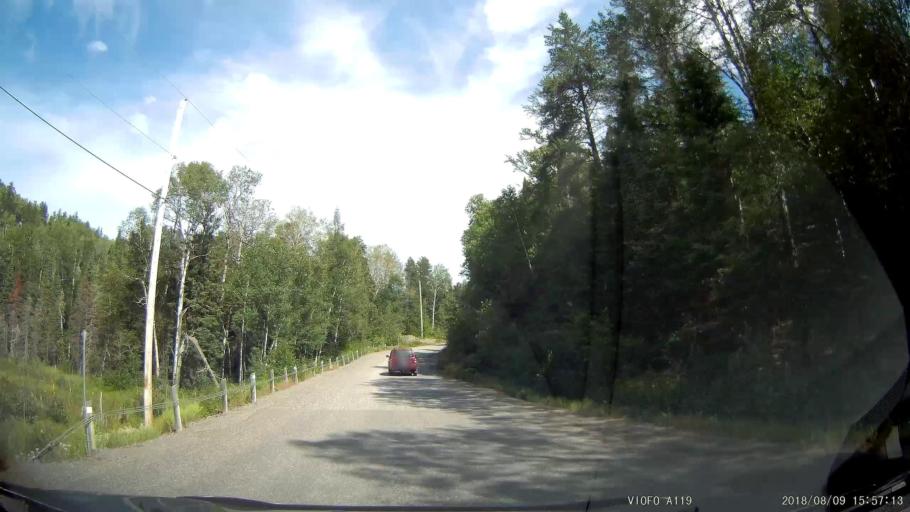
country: CA
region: Ontario
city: Rayside-Balfour
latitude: 46.6075
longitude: -81.5080
